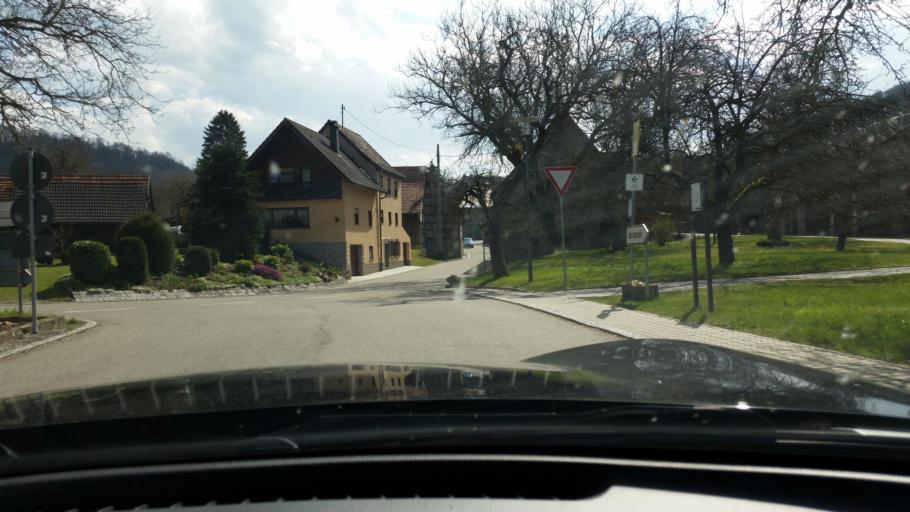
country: DE
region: Baden-Wuerttemberg
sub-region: Regierungsbezirk Stuttgart
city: Langenburg
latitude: 49.2661
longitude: 9.8374
